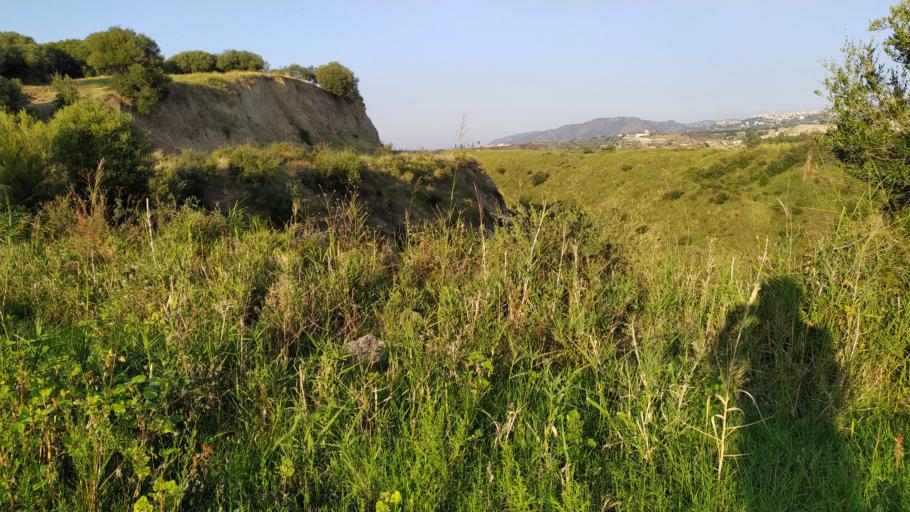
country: IT
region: Sicily
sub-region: Messina
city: Saponara Marittima
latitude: 38.2252
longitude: 15.4312
